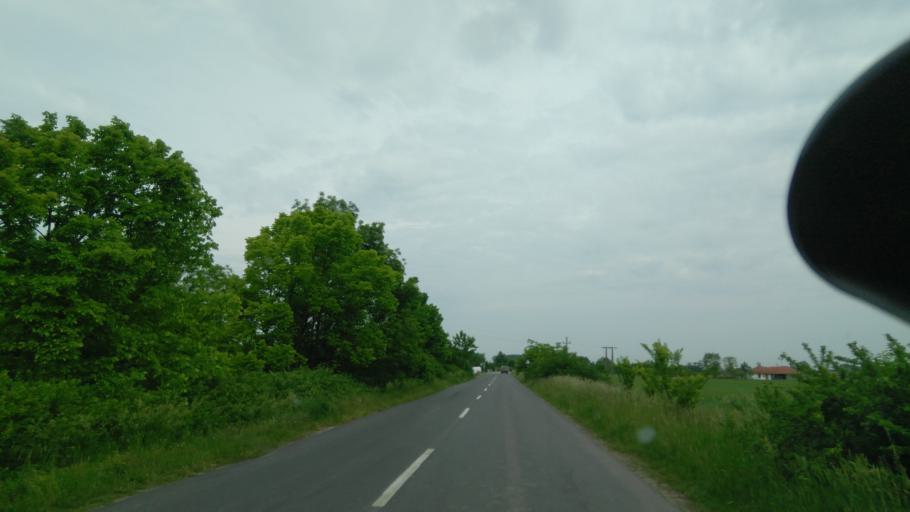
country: HU
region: Bekes
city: Szeghalom
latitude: 46.9898
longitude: 21.1811
